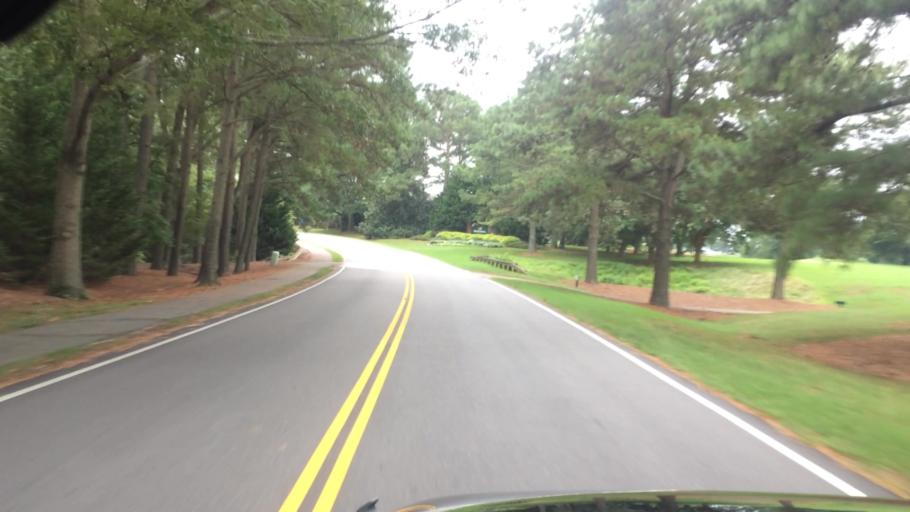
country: US
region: Virginia
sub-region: City of Williamsburg
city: Williamsburg
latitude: 37.2296
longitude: -76.6655
